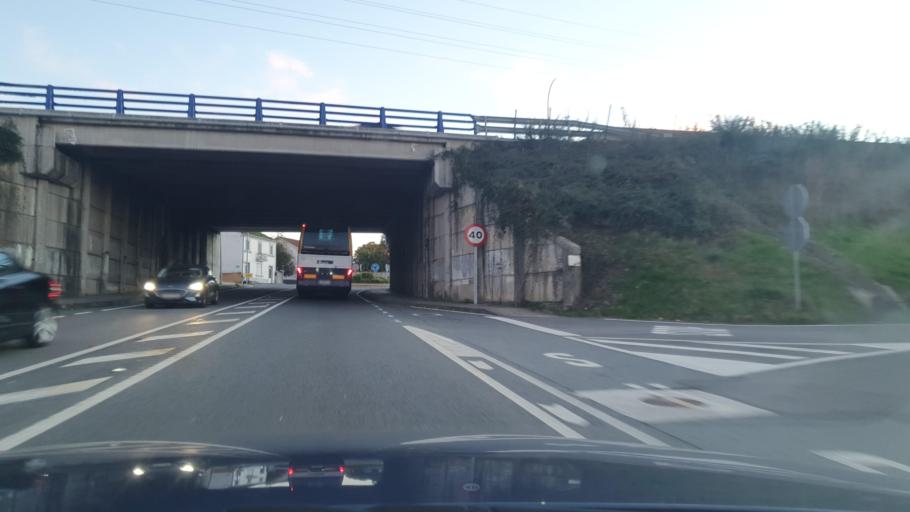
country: ES
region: Galicia
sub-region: Provincia da Coruna
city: Santiago de Compostela
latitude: 42.8536
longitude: -8.5393
